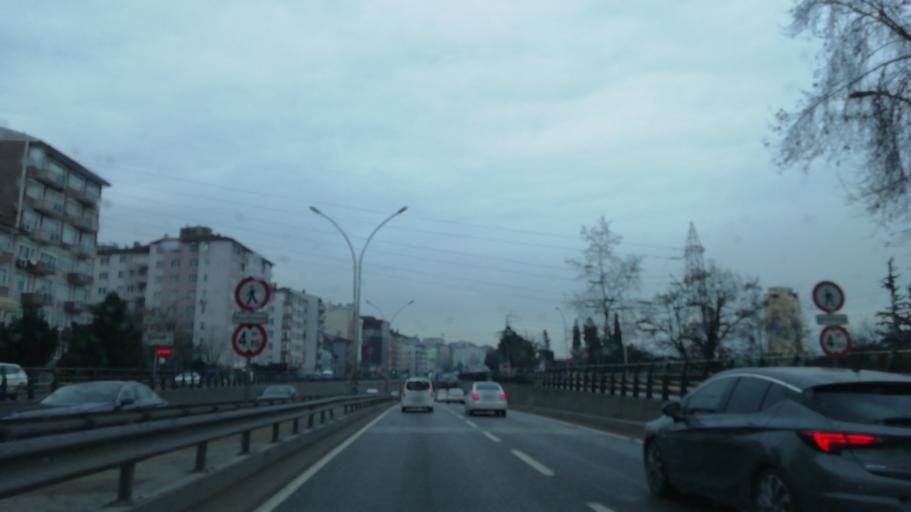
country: TR
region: Kocaeli
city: Izmit
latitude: 40.7664
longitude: 29.9063
